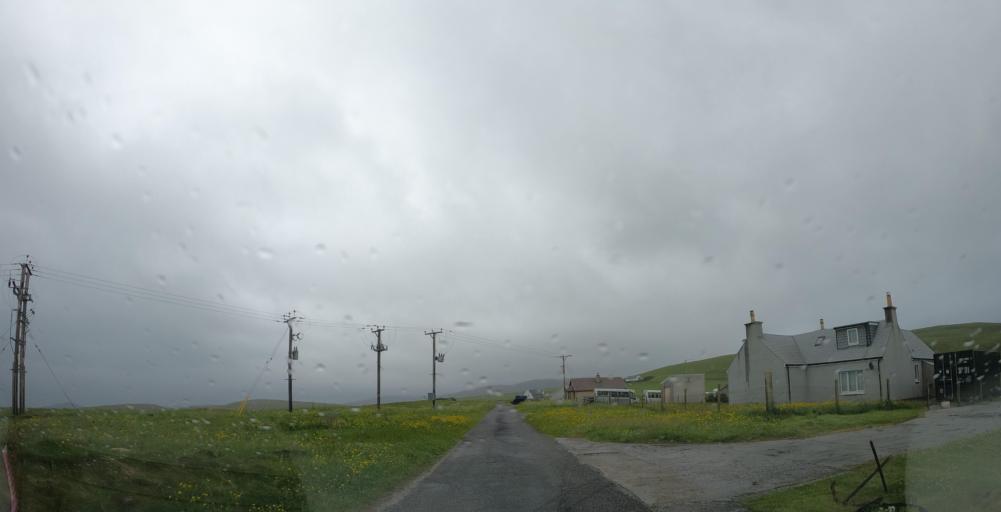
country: GB
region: Scotland
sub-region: Eilean Siar
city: Barra
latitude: 57.0400
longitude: -7.4245
